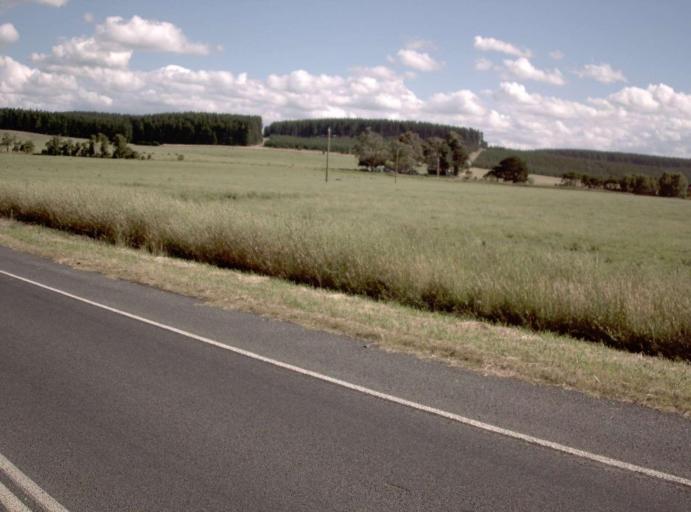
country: AU
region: Victoria
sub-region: Latrobe
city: Morwell
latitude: -38.1690
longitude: 146.4128
